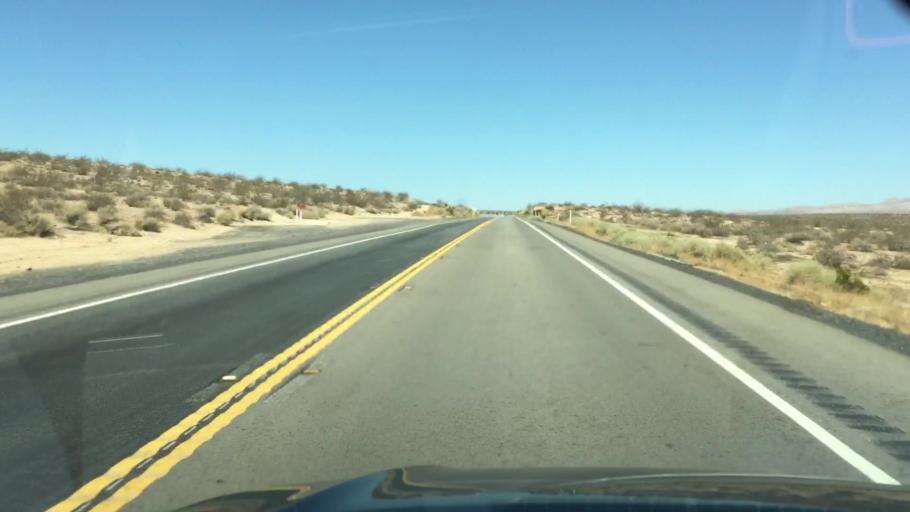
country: US
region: California
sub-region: Kern County
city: Boron
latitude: 35.0652
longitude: -117.5598
